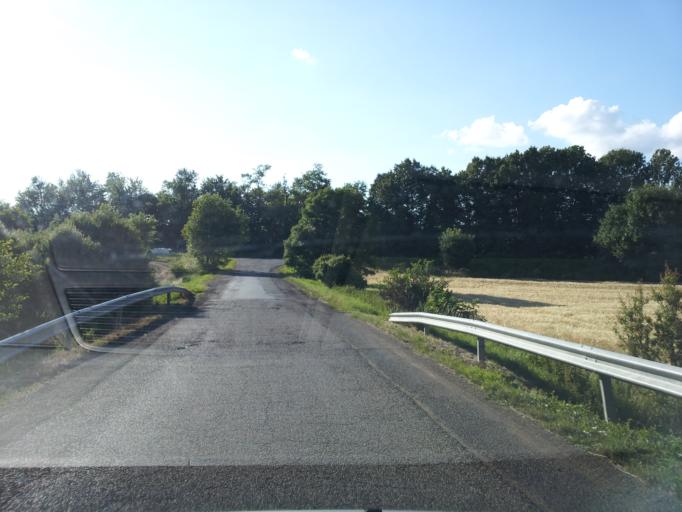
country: HU
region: Veszprem
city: Zirc
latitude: 47.2258
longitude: 17.8287
